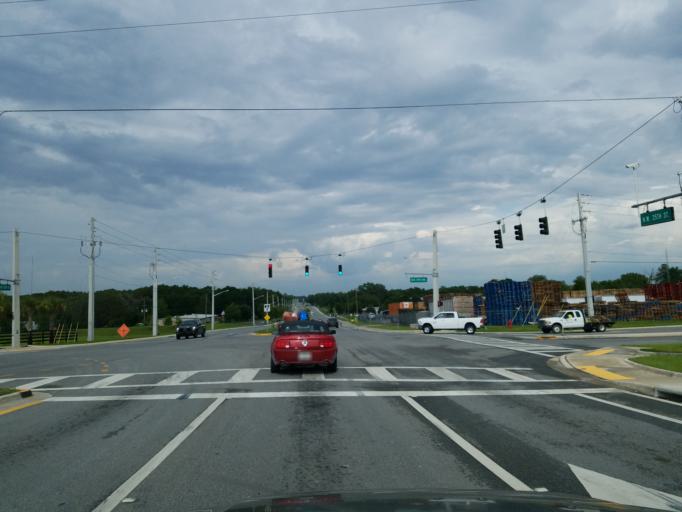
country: US
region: Florida
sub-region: Marion County
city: Ocala
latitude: 29.2233
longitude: -82.1690
